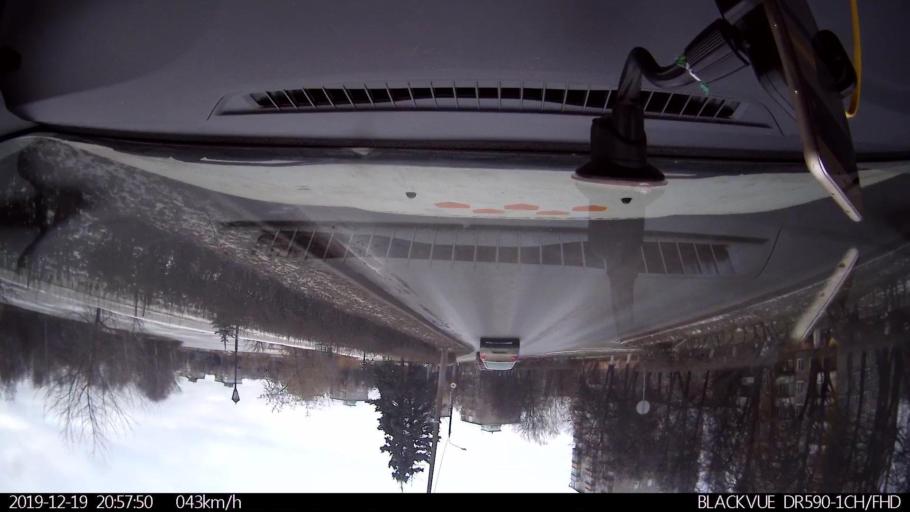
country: RU
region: Nizjnij Novgorod
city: Gorbatovka
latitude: 56.3432
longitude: 43.8492
